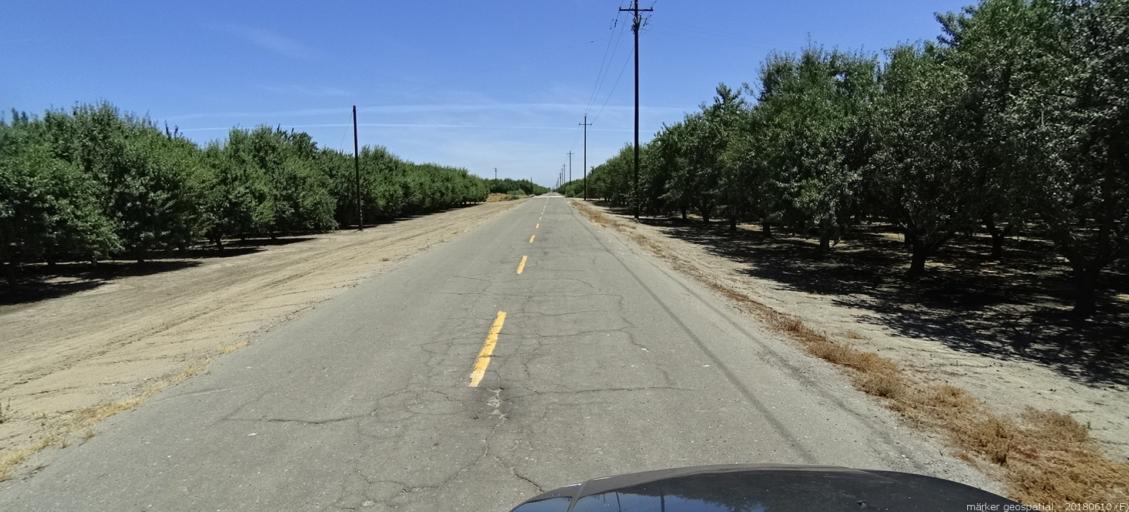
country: US
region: California
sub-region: Madera County
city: Chowchilla
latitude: 37.0545
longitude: -120.2863
